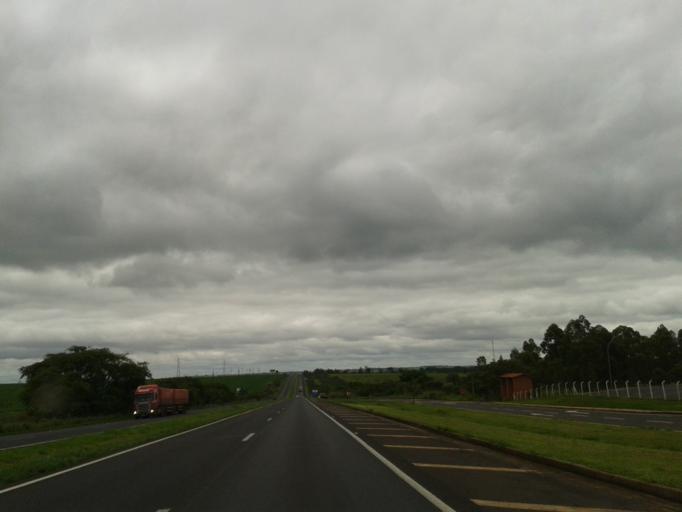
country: BR
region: Minas Gerais
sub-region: Uberlandia
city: Uberlandia
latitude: -19.0366
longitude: -48.2004
